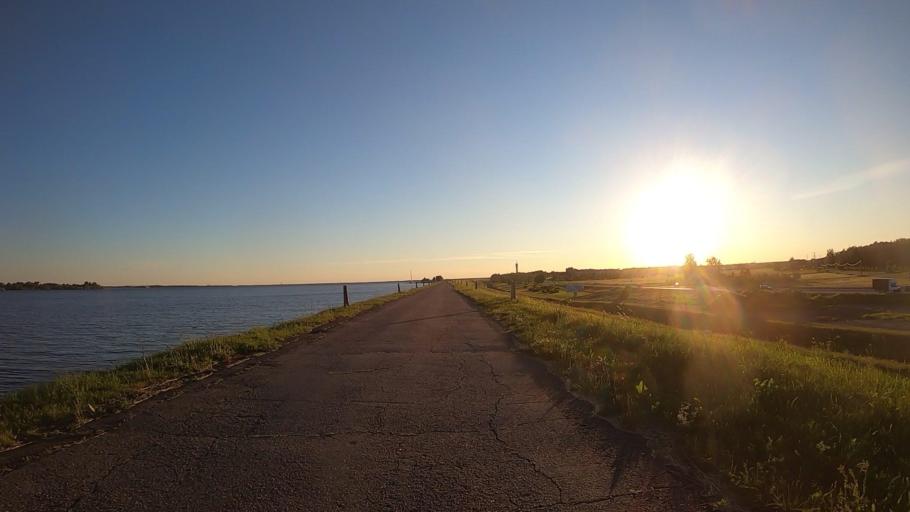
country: LV
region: Salaspils
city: Salaspils
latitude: 56.8457
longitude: 24.3628
